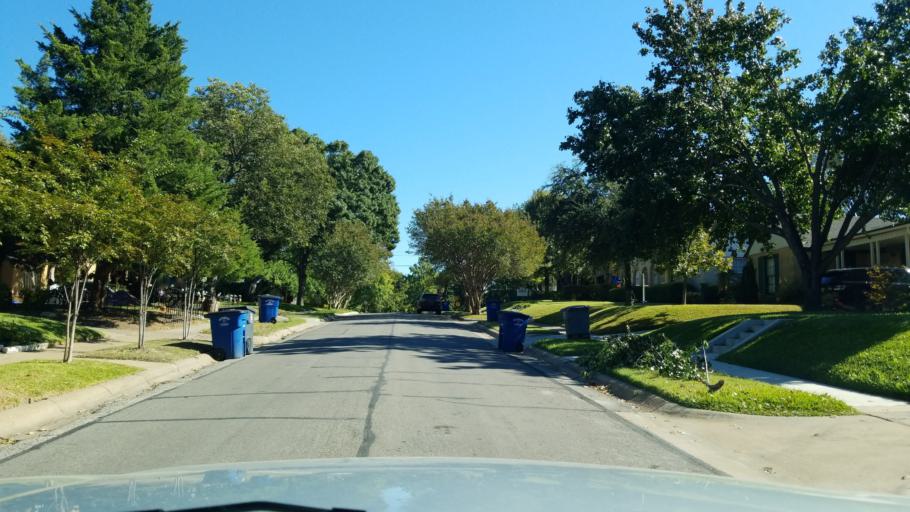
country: US
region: Texas
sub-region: Dallas County
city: Highland Park
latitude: 32.8060
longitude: -96.7415
